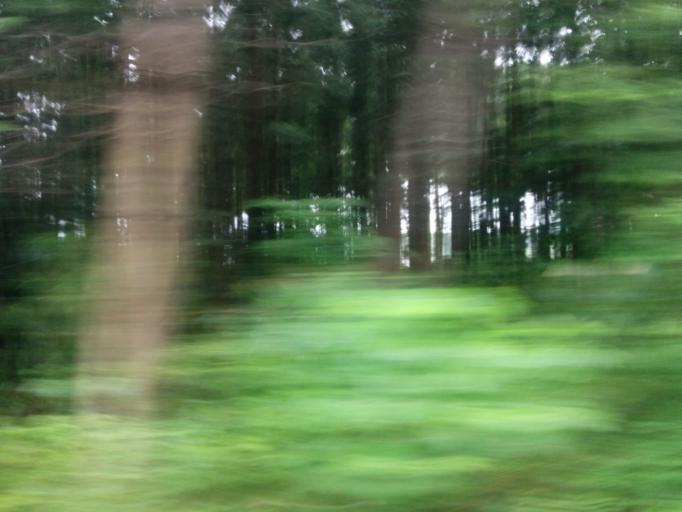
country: JP
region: Tochigi
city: Kanuma
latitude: 36.5891
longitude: 139.7531
